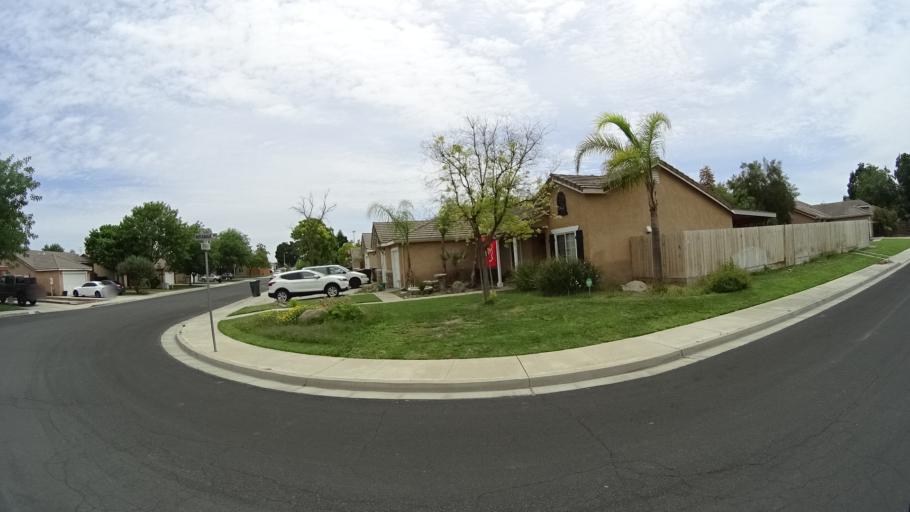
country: US
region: California
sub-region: Kings County
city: Lucerne
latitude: 36.3667
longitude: -119.6399
